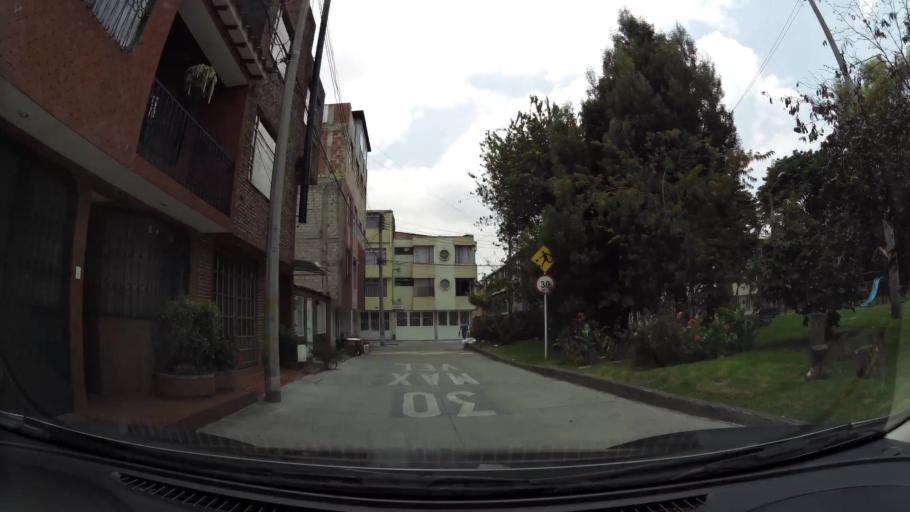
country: CO
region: Cundinamarca
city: Cota
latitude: 4.7457
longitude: -74.0620
